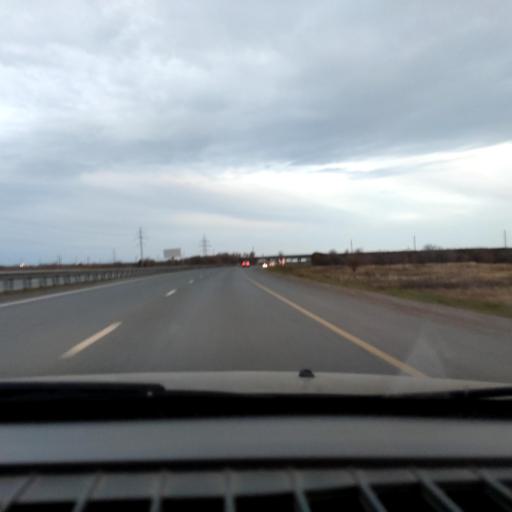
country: RU
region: Samara
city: Tol'yatti
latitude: 53.5660
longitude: 49.4934
